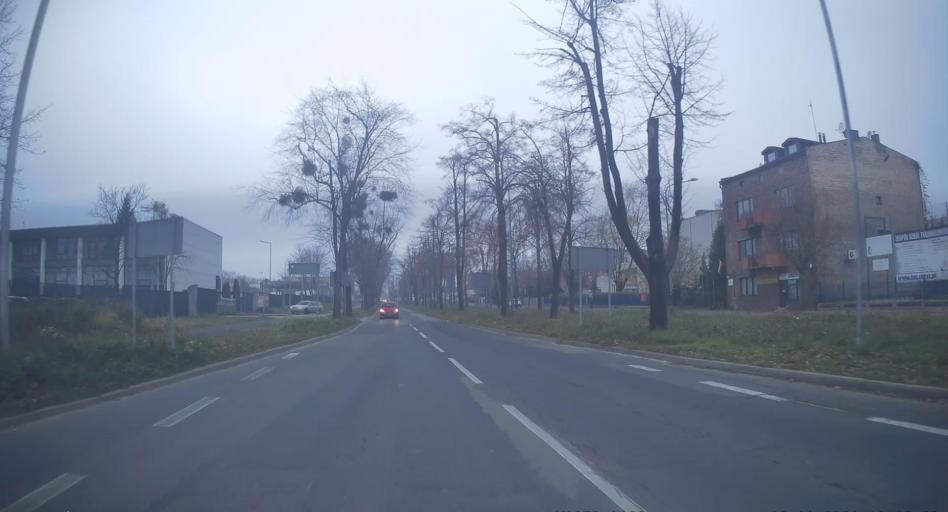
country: PL
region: Silesian Voivodeship
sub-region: Czestochowa
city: Czestochowa
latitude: 50.8168
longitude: 19.1032
